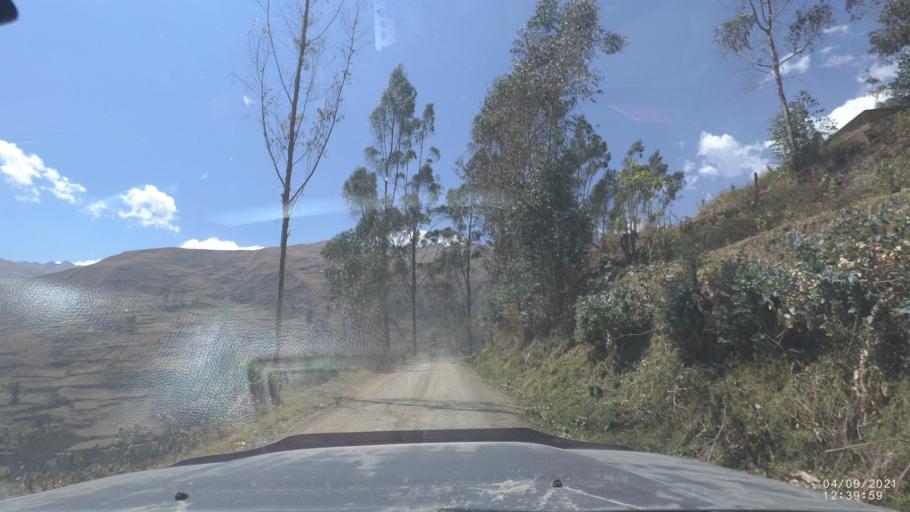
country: BO
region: Cochabamba
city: Colchani
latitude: -17.2298
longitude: -66.4982
